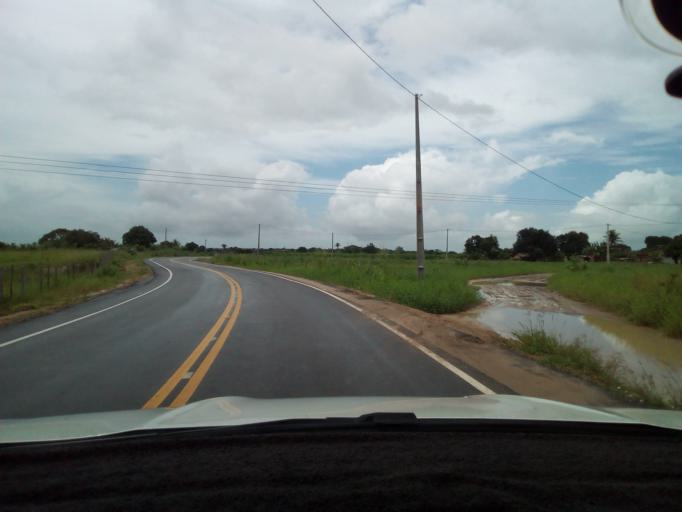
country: BR
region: Paraiba
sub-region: Pedras De Fogo
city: Pedras de Fogo
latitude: -7.3922
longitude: -35.1462
